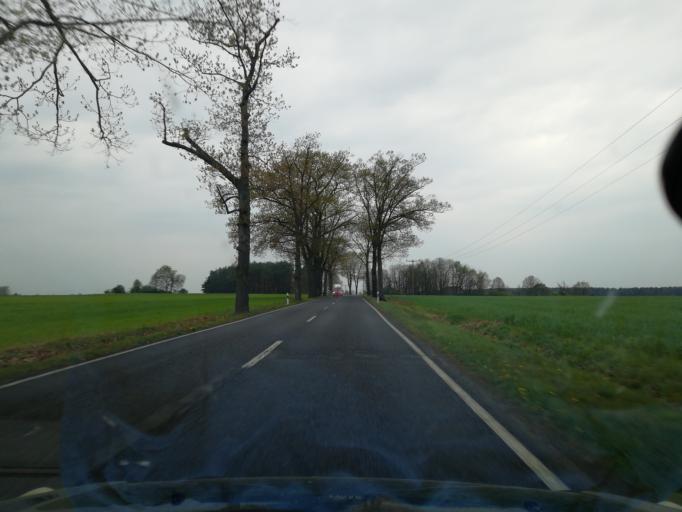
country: DE
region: Brandenburg
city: Calau
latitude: 51.7556
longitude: 13.9266
